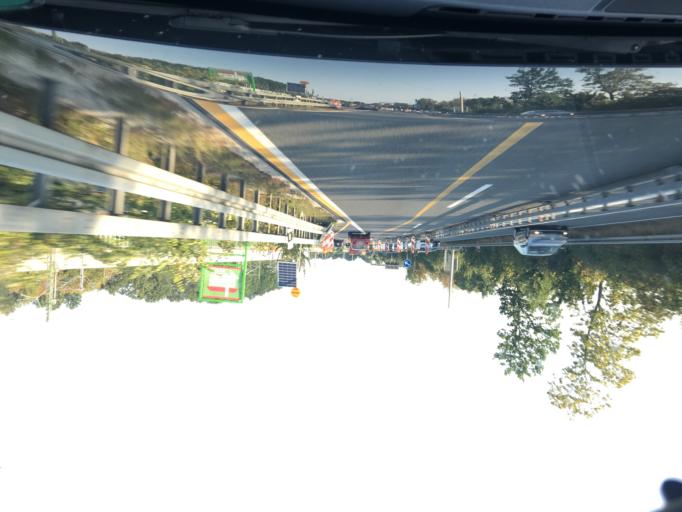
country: DE
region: Bavaria
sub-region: Regierungsbezirk Mittelfranken
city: Mohrendorf
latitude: 49.6148
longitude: 11.0010
